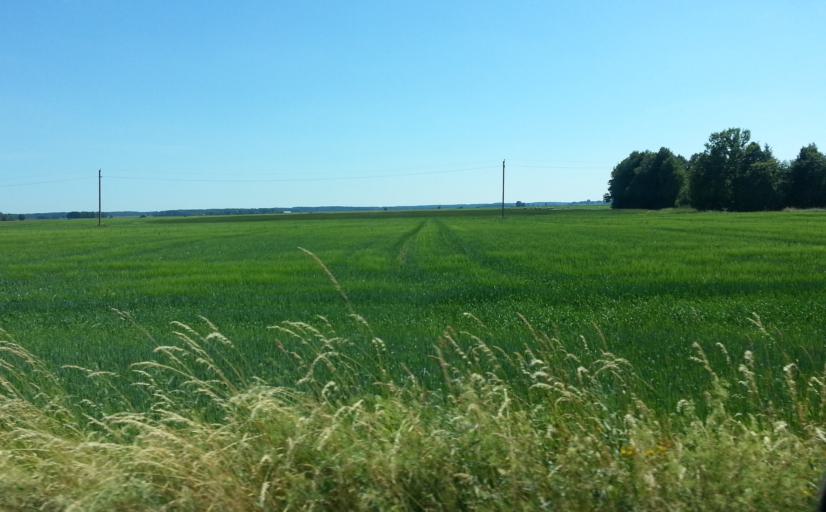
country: LT
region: Panevezys
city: Pasvalys
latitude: 56.2249
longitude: 24.4986
